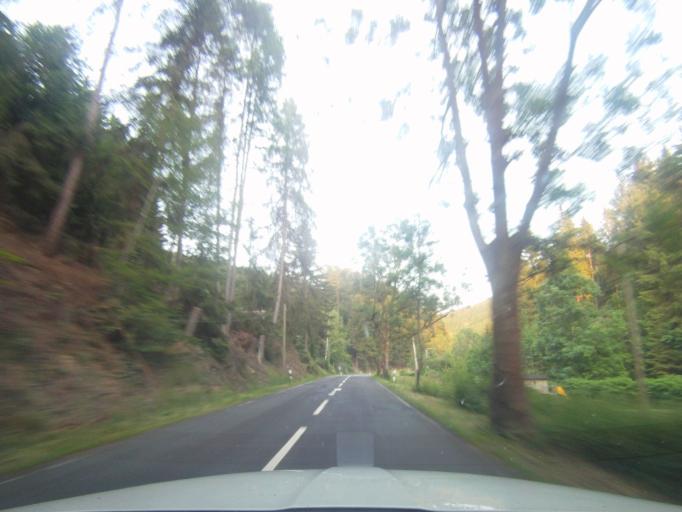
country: DE
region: Thuringia
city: Eisfeld
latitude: 50.4848
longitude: 10.8934
